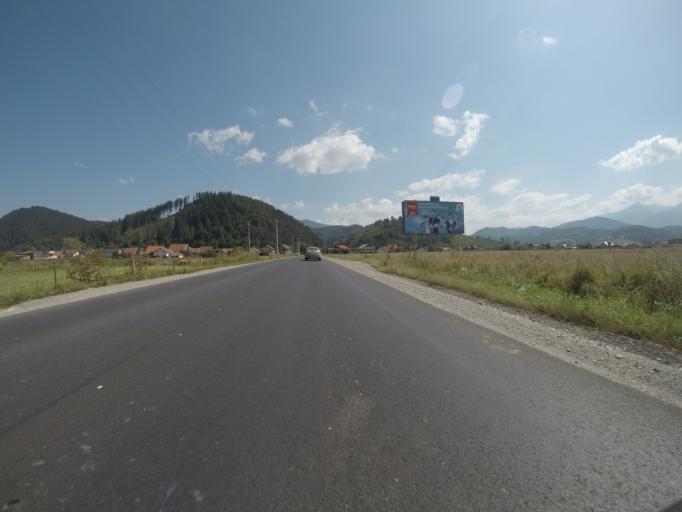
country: RO
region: Brasov
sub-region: Oras Rasnov
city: Rasnov
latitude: 45.5781
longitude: 25.4524
